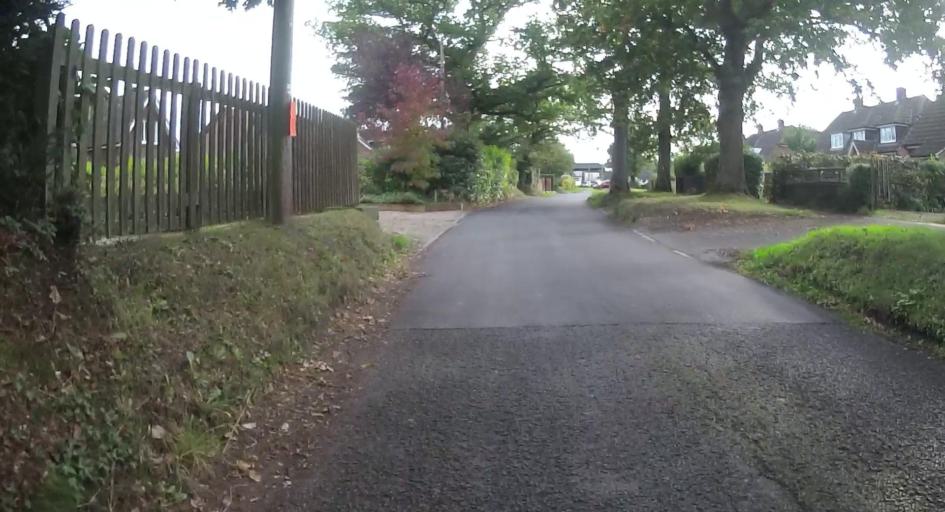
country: GB
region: England
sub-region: West Berkshire
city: Thatcham
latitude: 51.4157
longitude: -1.2241
